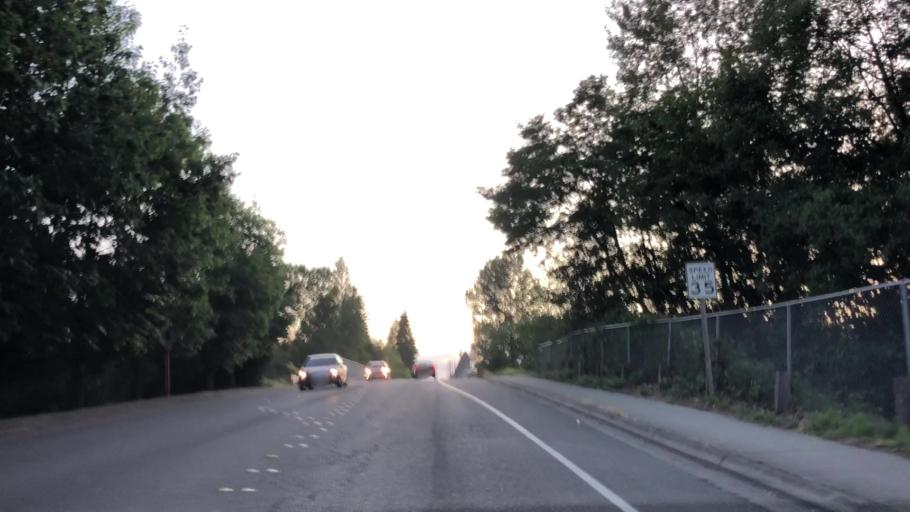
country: US
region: Washington
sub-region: Snohomish County
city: Martha Lake
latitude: 47.8641
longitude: -122.2731
